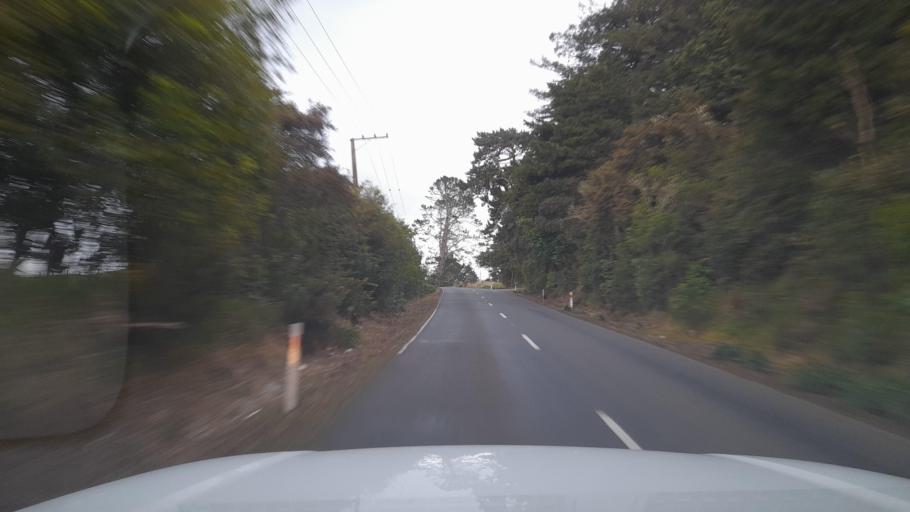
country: NZ
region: Northland
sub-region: Whangarei
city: Maungatapere
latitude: -35.7436
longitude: 174.2060
